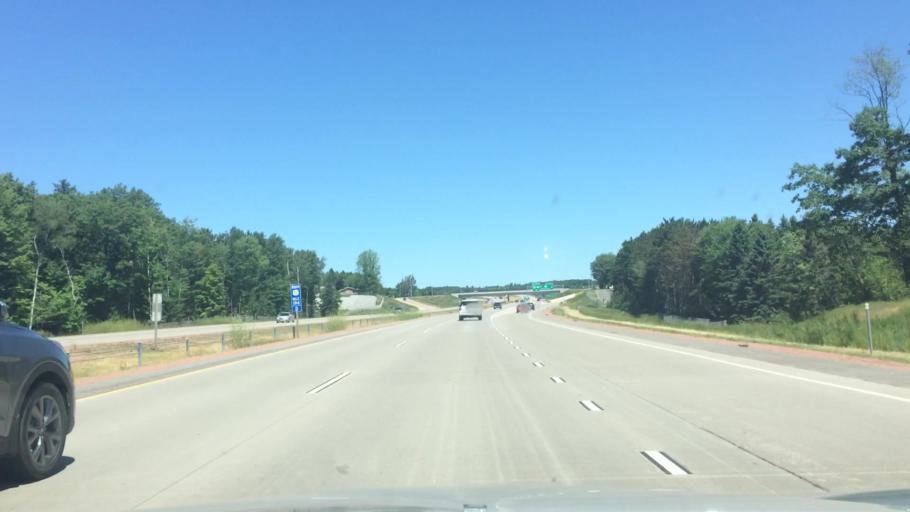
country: US
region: Wisconsin
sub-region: Marathon County
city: Wausau
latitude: 44.9803
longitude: -89.6572
